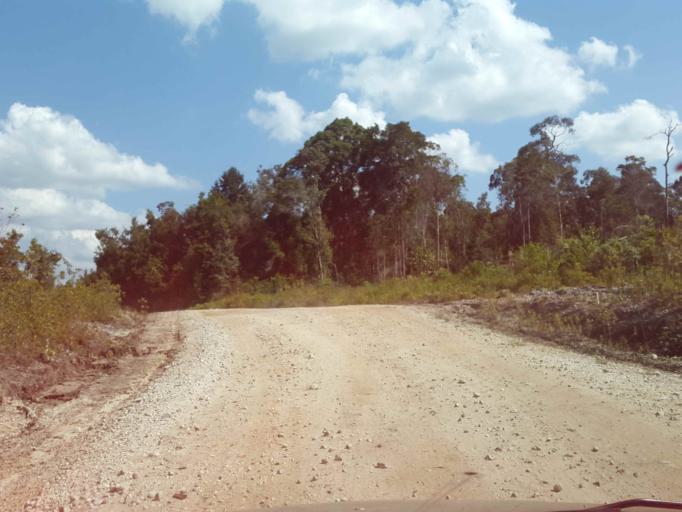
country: MY
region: Sarawak
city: Simanggang
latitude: 0.7483
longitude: 111.5729
